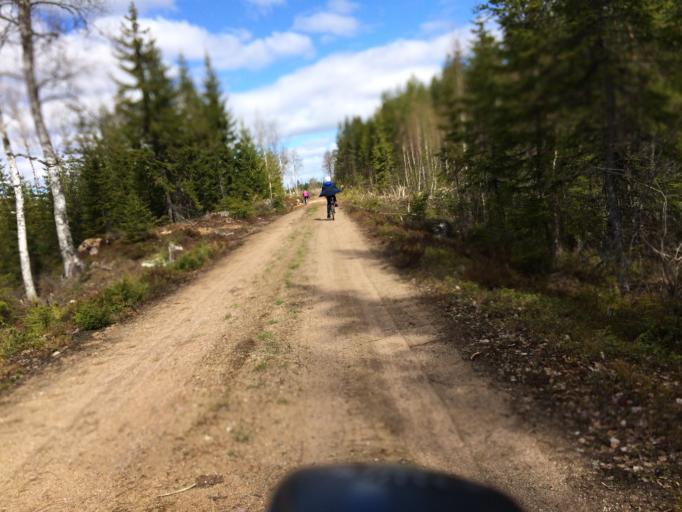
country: SE
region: OErebro
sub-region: Hallefors Kommun
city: Haellefors
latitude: 60.0481
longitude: 14.5262
